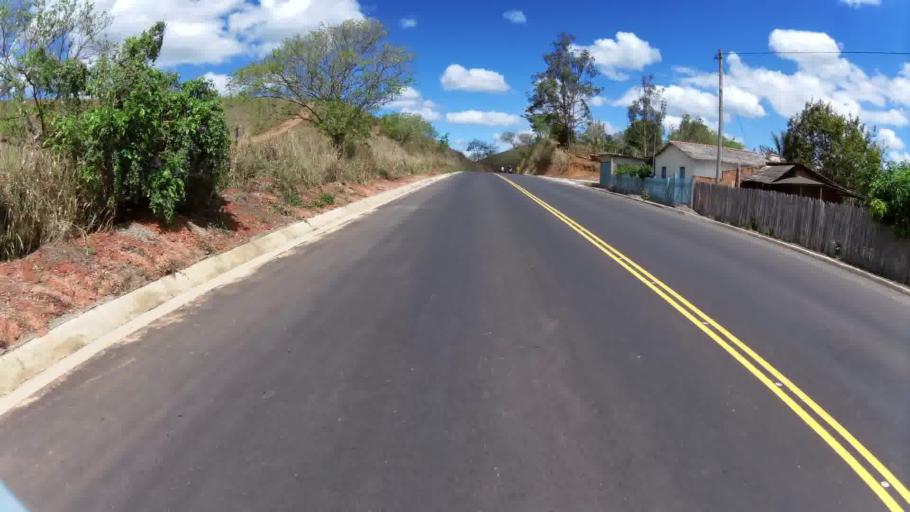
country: BR
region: Rio de Janeiro
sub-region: Itaperuna
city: Itaperuna
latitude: -21.2630
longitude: -41.7712
